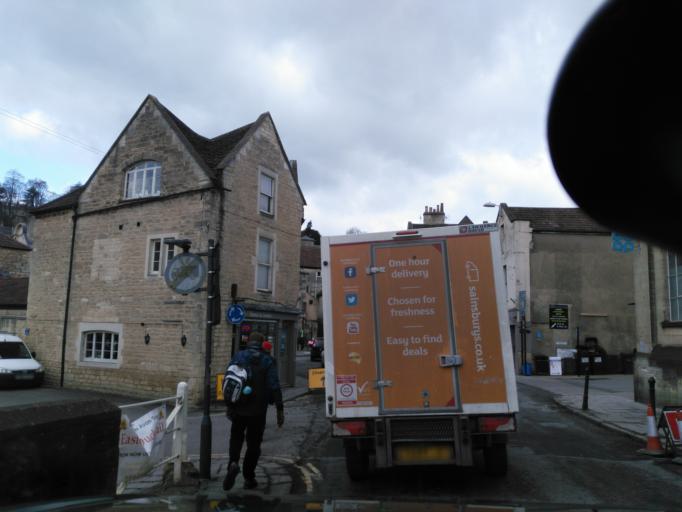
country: GB
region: England
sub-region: Wiltshire
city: Bradford-on-Avon
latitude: 51.3472
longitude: -2.2508
